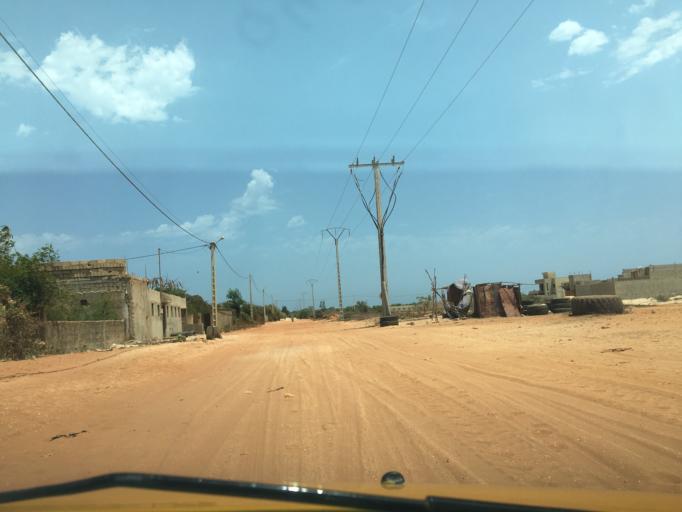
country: SN
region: Thies
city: Thies
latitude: 14.8106
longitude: -17.1909
